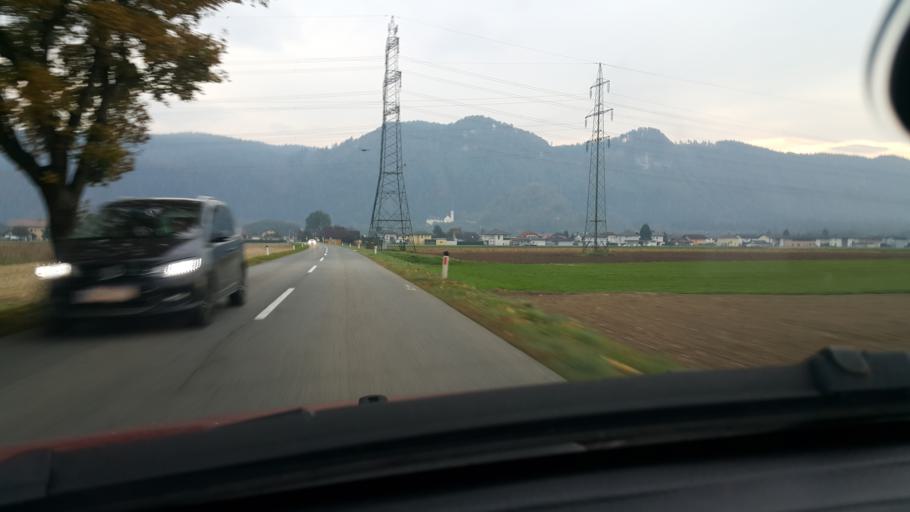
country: AT
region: Carinthia
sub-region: Politischer Bezirk Klagenfurt Land
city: Ebenthal
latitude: 46.6152
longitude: 14.3982
